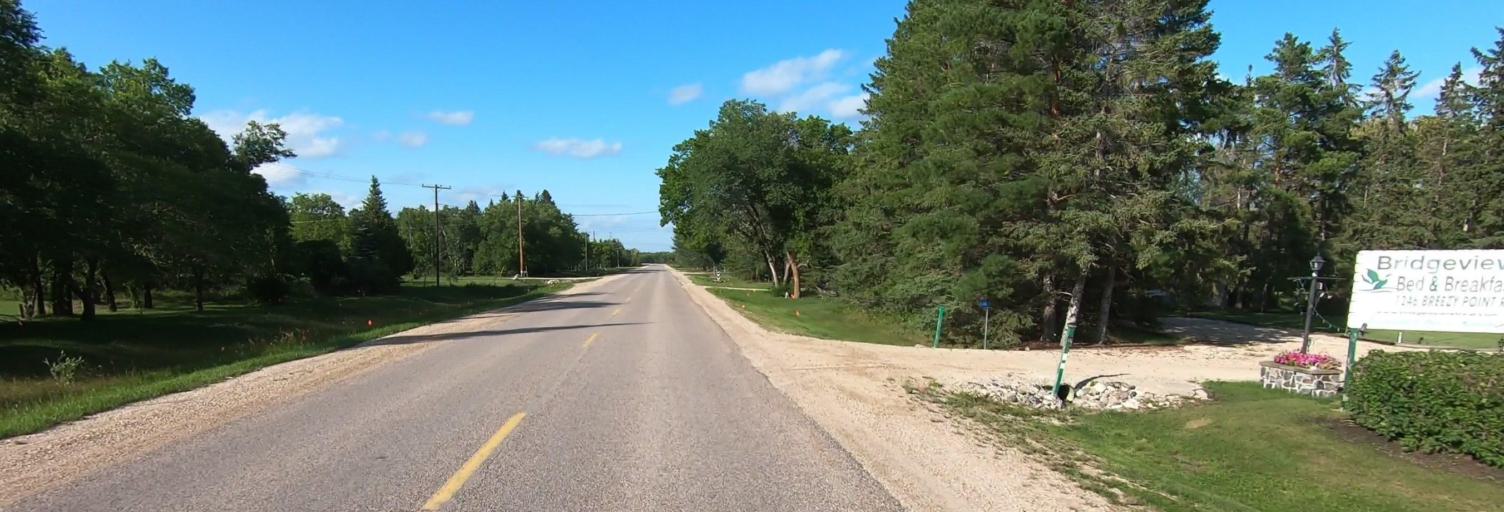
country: CA
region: Manitoba
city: Selkirk
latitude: 50.1951
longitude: -96.8427
